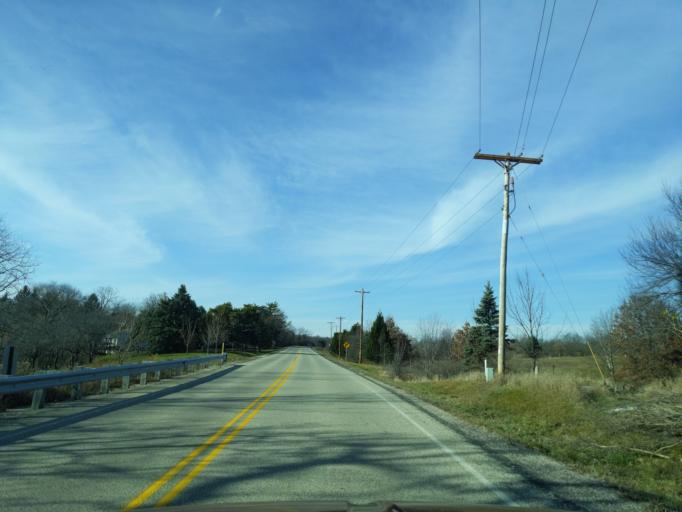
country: US
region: Wisconsin
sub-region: Walworth County
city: Elkhorn
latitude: 42.7529
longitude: -88.5966
